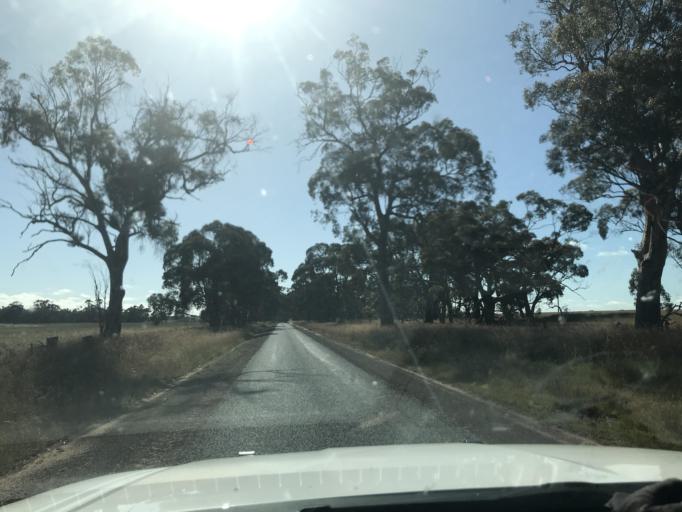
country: AU
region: Victoria
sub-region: Horsham
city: Horsham
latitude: -37.0253
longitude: 141.7058
